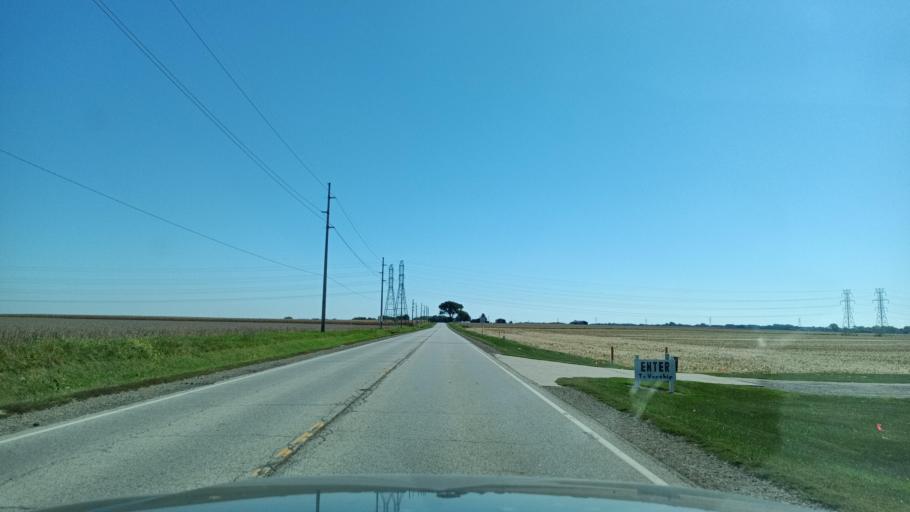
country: US
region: Illinois
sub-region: Peoria County
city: Dunlap
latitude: 40.7886
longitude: -89.7413
